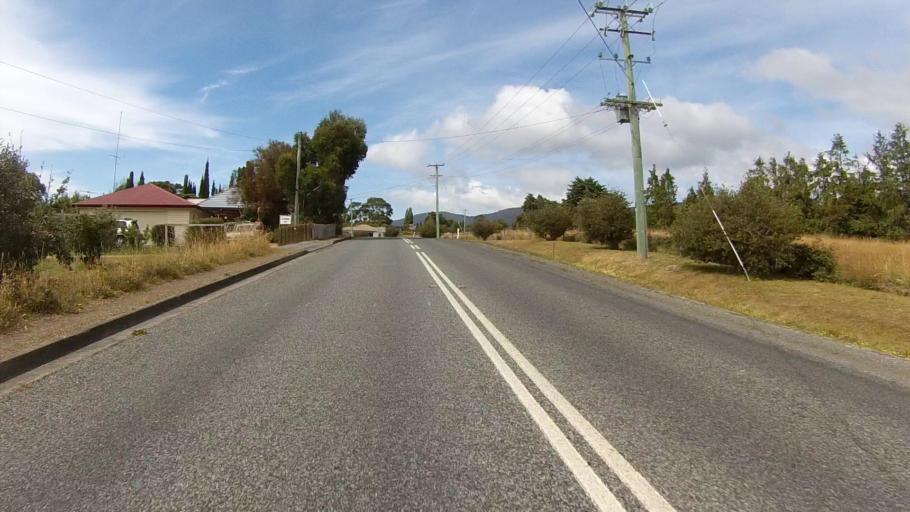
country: AU
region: Tasmania
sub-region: Kingborough
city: Kettering
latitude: -43.1548
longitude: 147.2378
